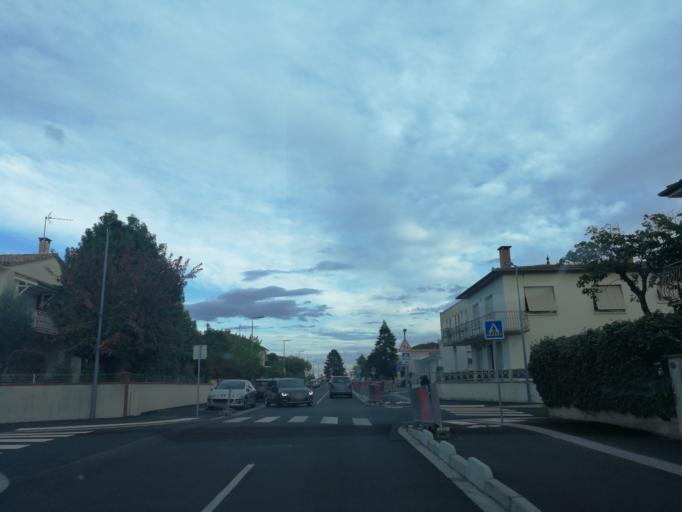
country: FR
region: Midi-Pyrenees
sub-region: Departement de la Haute-Garonne
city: L'Union
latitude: 43.6581
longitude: 1.4775
